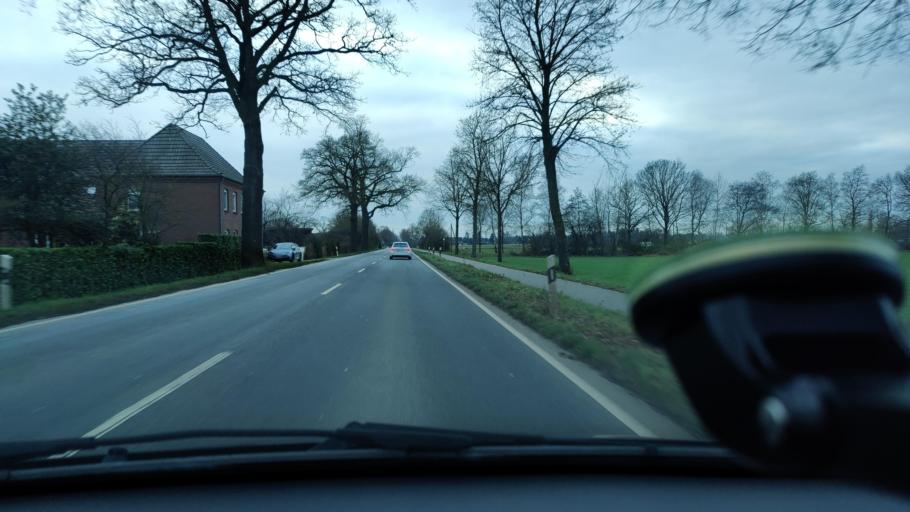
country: DE
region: North Rhine-Westphalia
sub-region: Regierungsbezirk Dusseldorf
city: Sonsbeck
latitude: 51.5789
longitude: 6.3792
